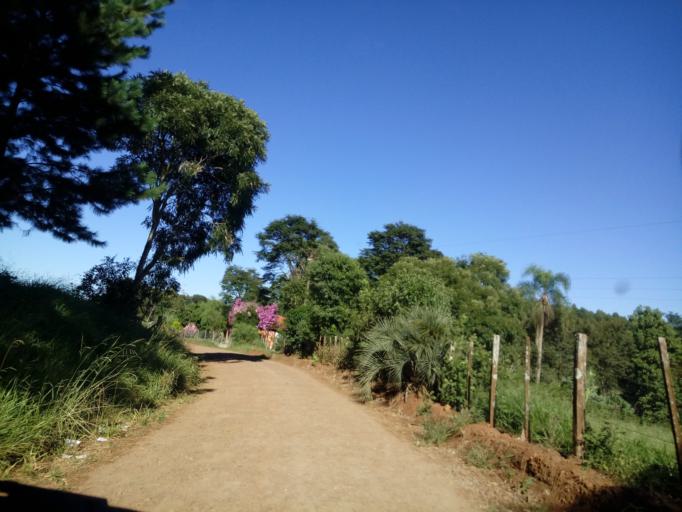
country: BR
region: Santa Catarina
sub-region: Chapeco
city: Chapeco
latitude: -27.1861
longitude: -52.7321
